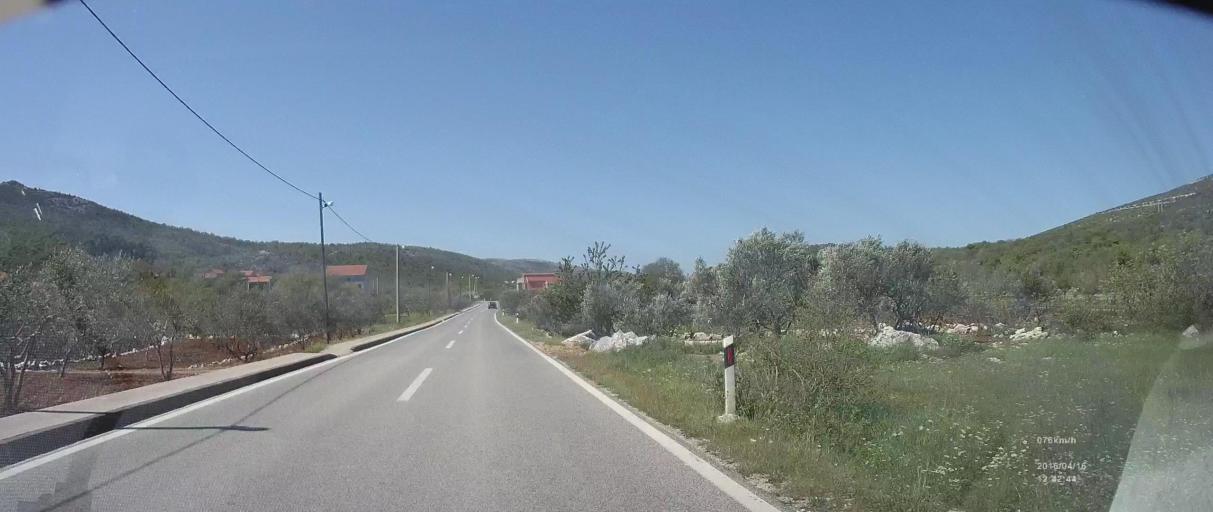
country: HR
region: Sibensko-Kniniska
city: Rogoznica
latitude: 43.6300
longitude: 16.0848
